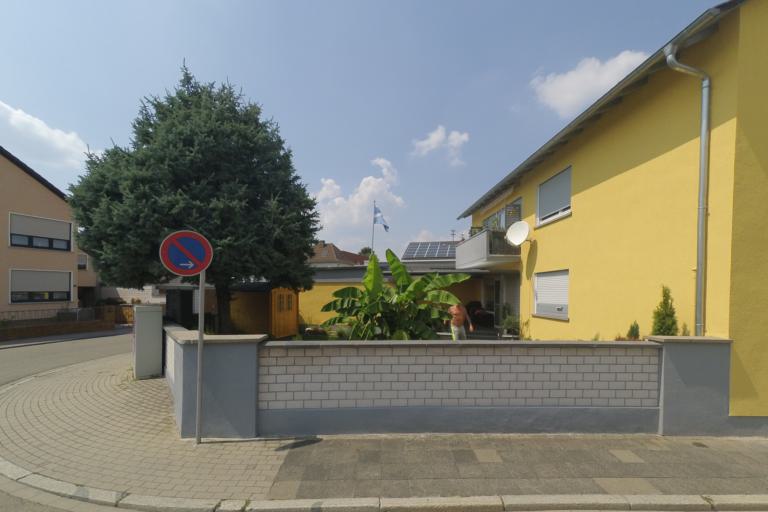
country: DE
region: Rheinland-Pfalz
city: Mutterstadt
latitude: 49.4525
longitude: 8.3785
